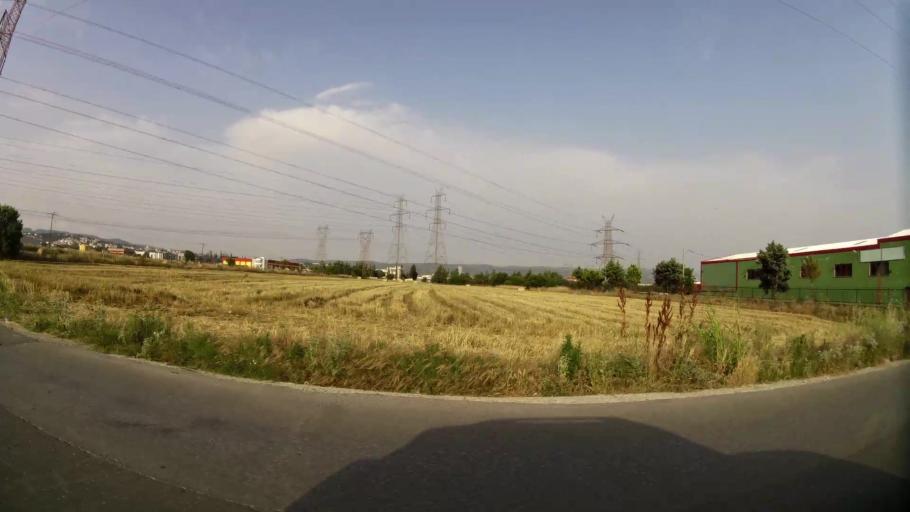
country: GR
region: Central Macedonia
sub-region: Nomos Thessalonikis
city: Oraiokastro
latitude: 40.7013
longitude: 22.9093
